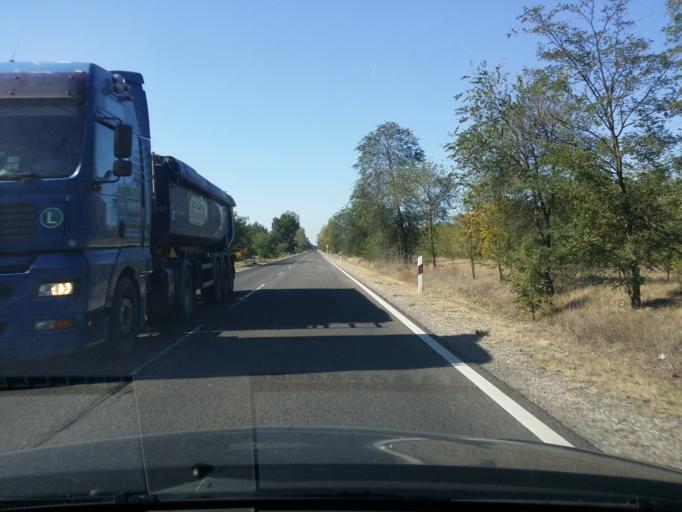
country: HU
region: Bacs-Kiskun
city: Nyarlorinc
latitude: 46.8629
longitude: 19.9292
